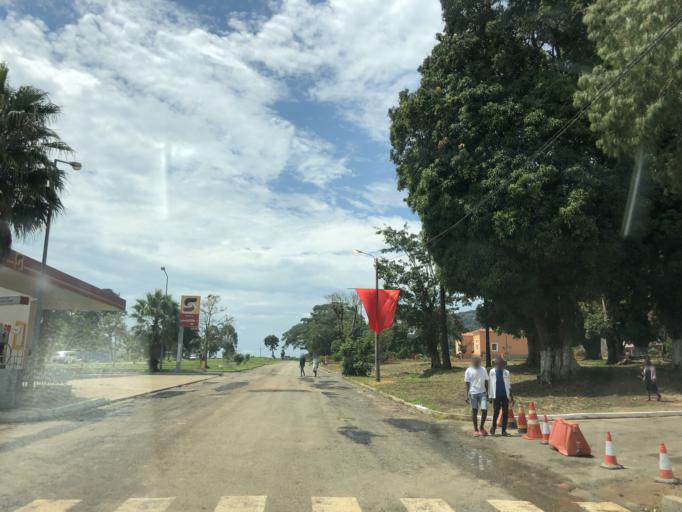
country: AO
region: Cuanza Sul
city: Quibala
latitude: -10.7372
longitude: 14.9799
